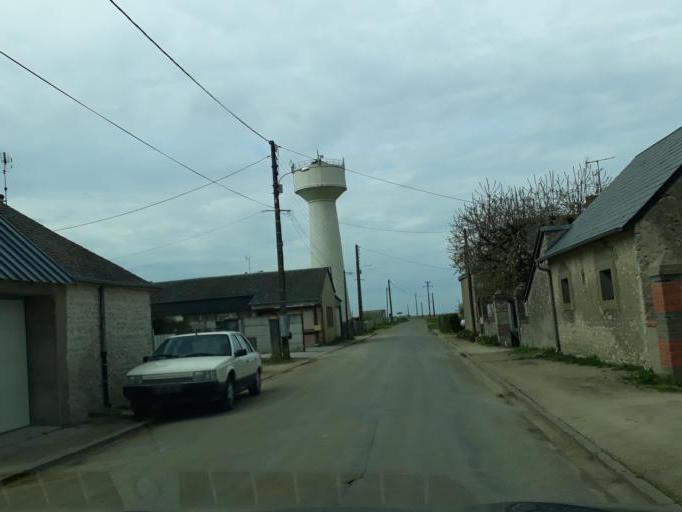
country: FR
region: Centre
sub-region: Departement du Loiret
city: Epieds-en-Beauce
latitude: 47.9297
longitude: 1.5755
